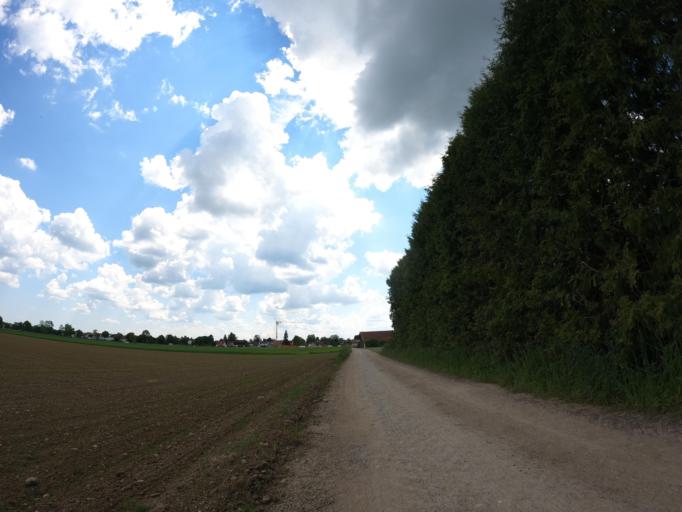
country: DE
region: Bavaria
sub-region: Upper Bavaria
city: Sauerlach
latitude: 47.9822
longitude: 11.6458
